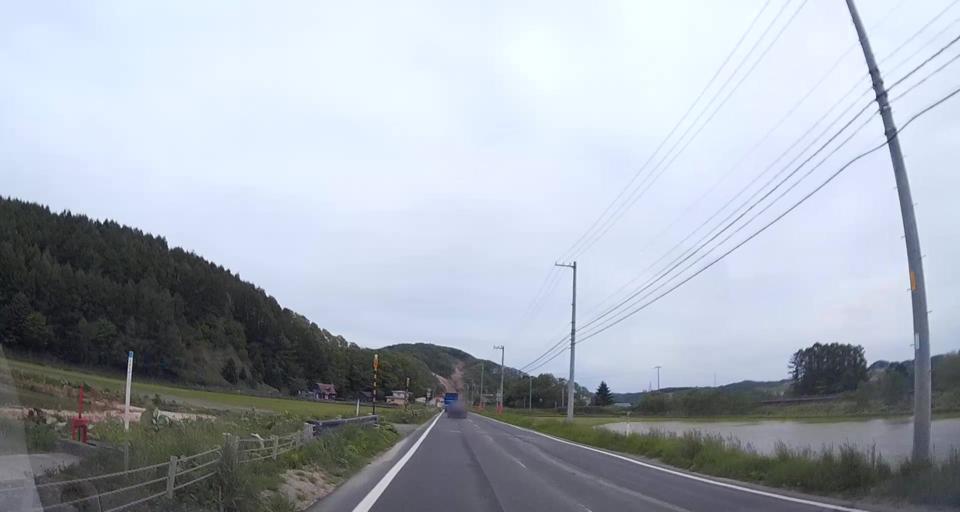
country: JP
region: Hokkaido
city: Chitose
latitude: 42.7583
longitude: 141.9221
